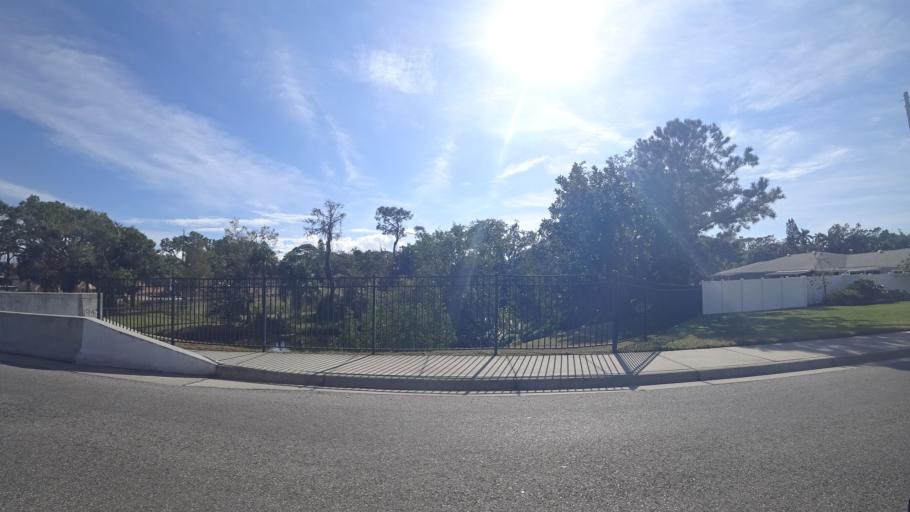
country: US
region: Florida
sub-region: Manatee County
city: Bradenton
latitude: 27.4919
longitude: -82.5815
